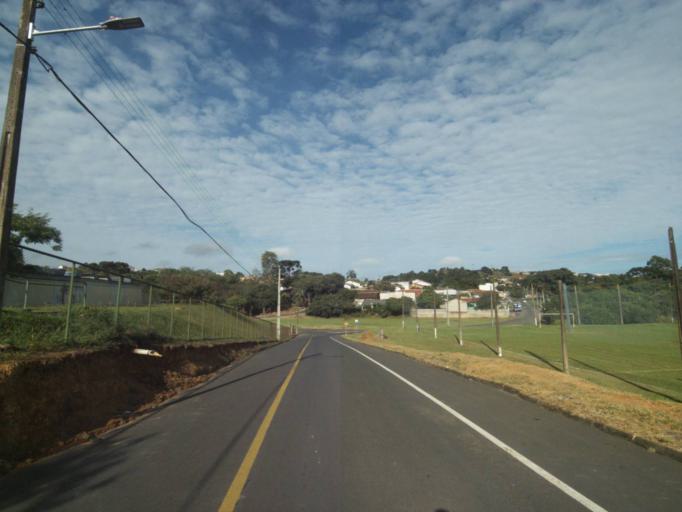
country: BR
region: Parana
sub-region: Telemaco Borba
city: Telemaco Borba
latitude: -24.3436
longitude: -50.6087
